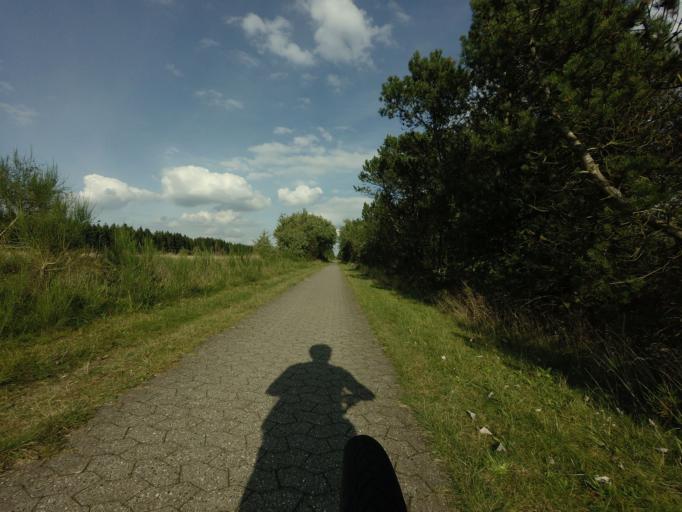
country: DK
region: Central Jutland
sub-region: Viborg Kommune
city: Karup
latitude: 56.3158
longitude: 9.1963
